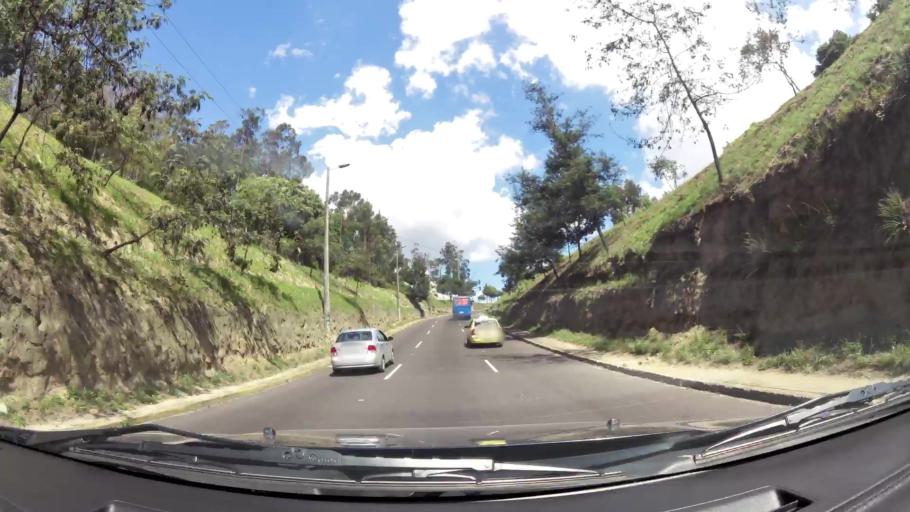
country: EC
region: Pichincha
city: Quito
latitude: -0.0984
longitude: -78.4701
